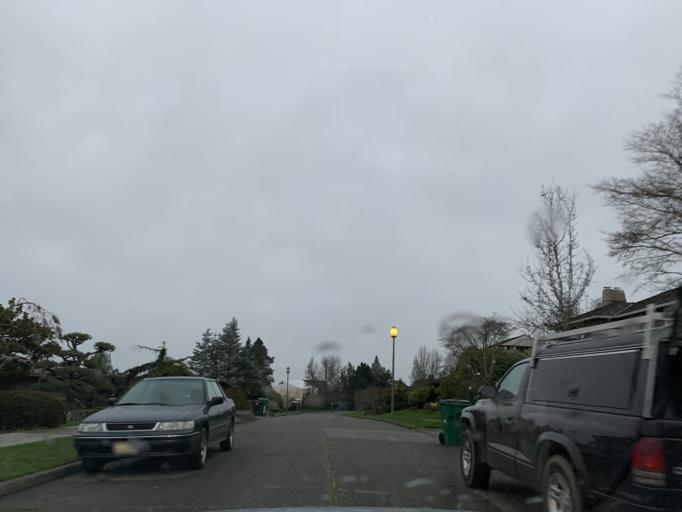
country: US
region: Washington
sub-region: King County
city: Yarrow Point
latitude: 47.6710
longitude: -122.2610
